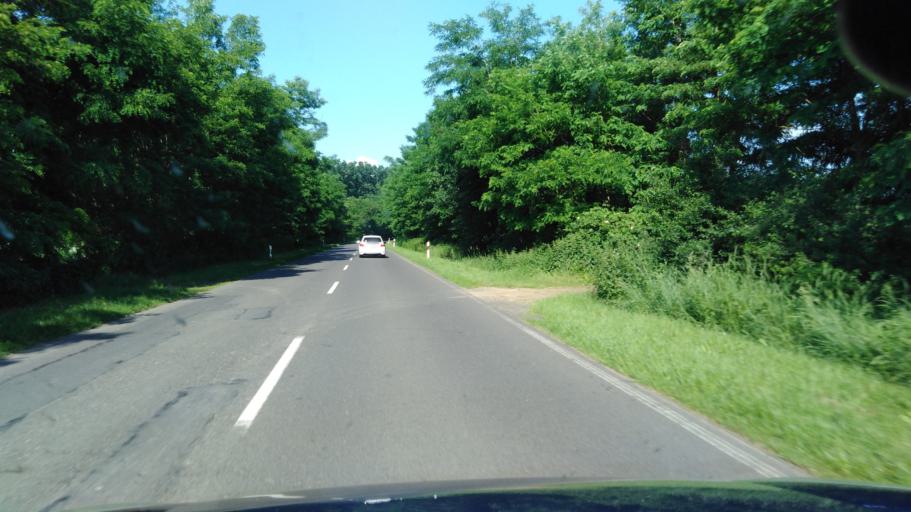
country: HU
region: Szabolcs-Szatmar-Bereg
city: Nyirvasvari
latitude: 47.8111
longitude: 22.2189
